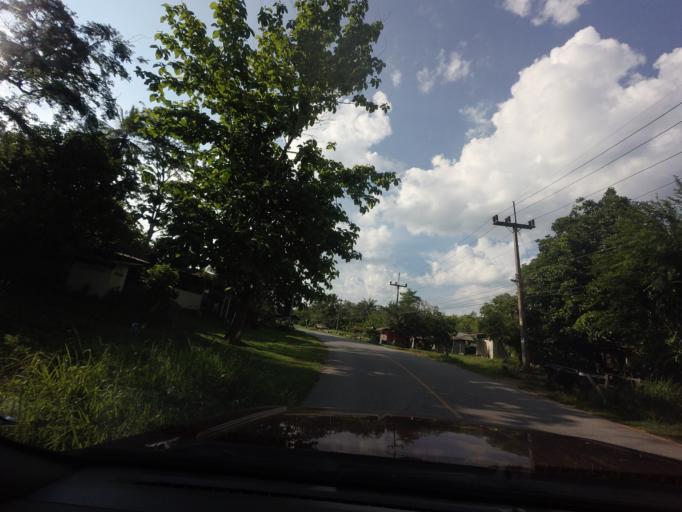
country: TH
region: Yala
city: Than To
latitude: 6.2018
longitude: 101.2376
